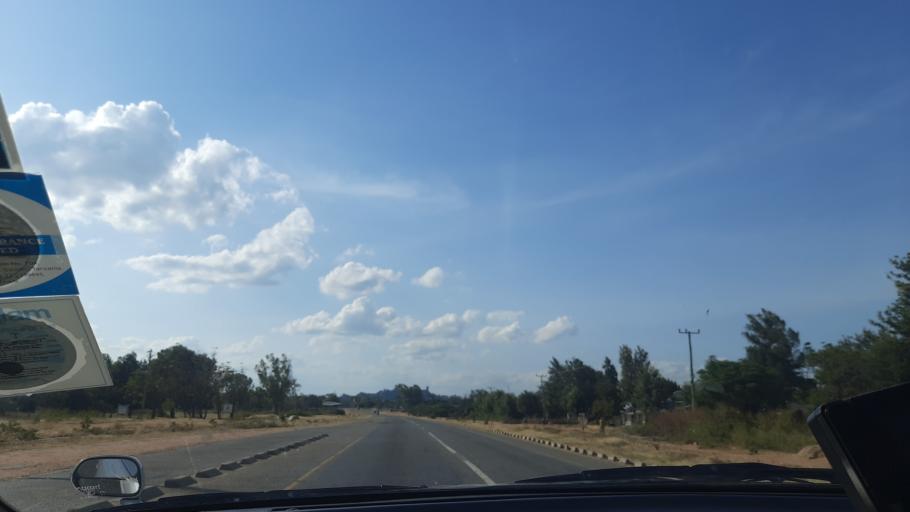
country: TZ
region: Singida
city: Puma
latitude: -5.0006
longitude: 34.7568
